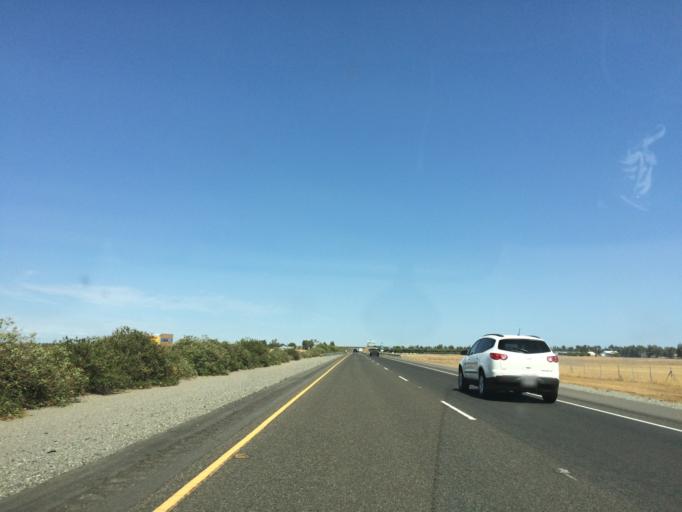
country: US
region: California
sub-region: Glenn County
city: Orland
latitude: 39.6877
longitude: -122.2047
